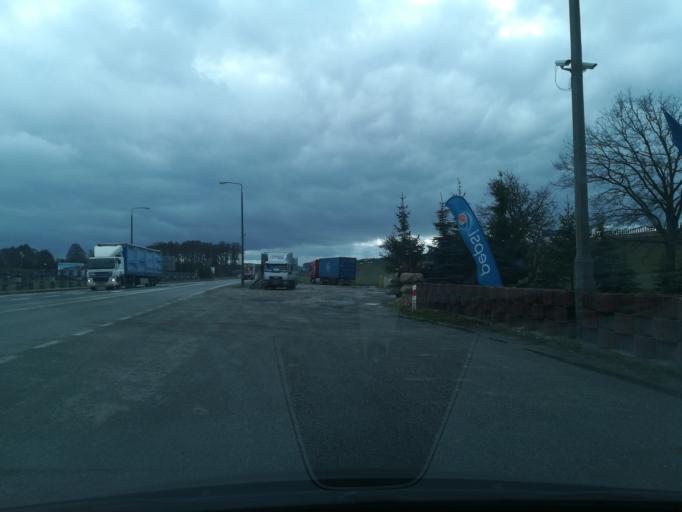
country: PL
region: Kujawsko-Pomorskie
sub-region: Powiat aleksandrowski
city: Ciechocinek
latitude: 52.8706
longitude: 18.7559
